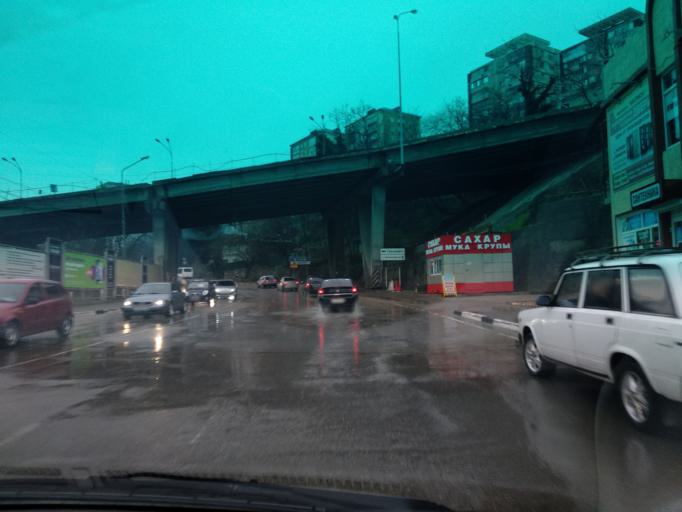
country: RU
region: Krasnodarskiy
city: Tuapse
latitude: 44.1054
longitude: 39.0866
